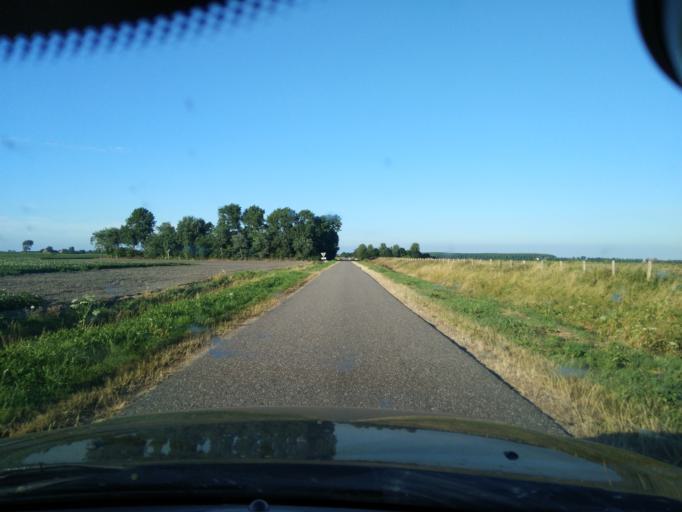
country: NL
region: Zeeland
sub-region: Schouwen-Duiveland
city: Scharendijke
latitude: 51.6836
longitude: 3.8633
